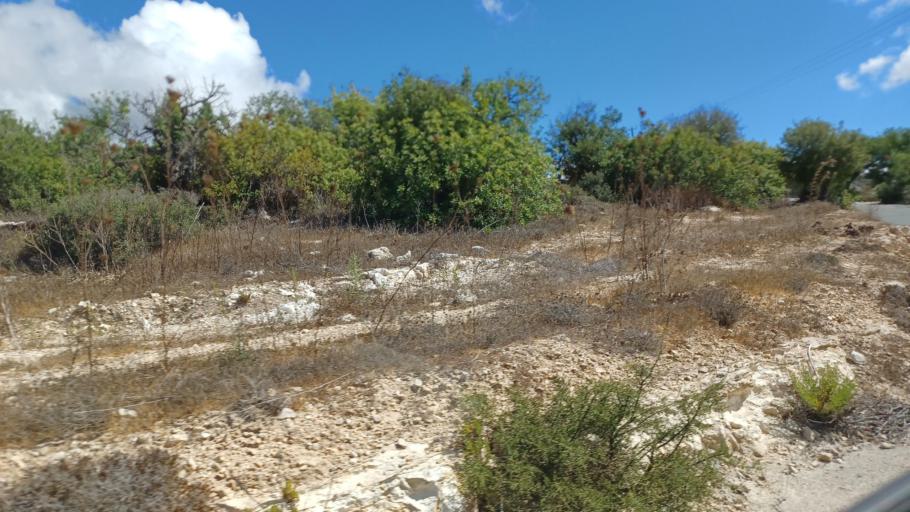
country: CY
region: Pafos
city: Tala
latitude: 34.8549
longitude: 32.4345
